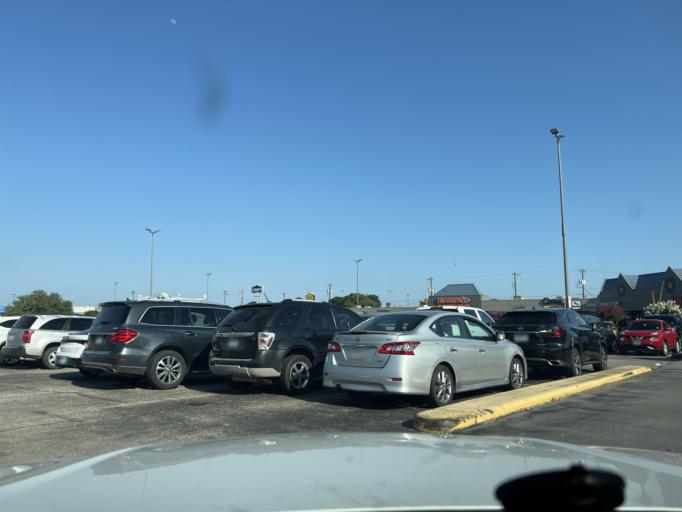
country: US
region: Texas
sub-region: Washington County
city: Brenham
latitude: 30.1411
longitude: -96.3978
